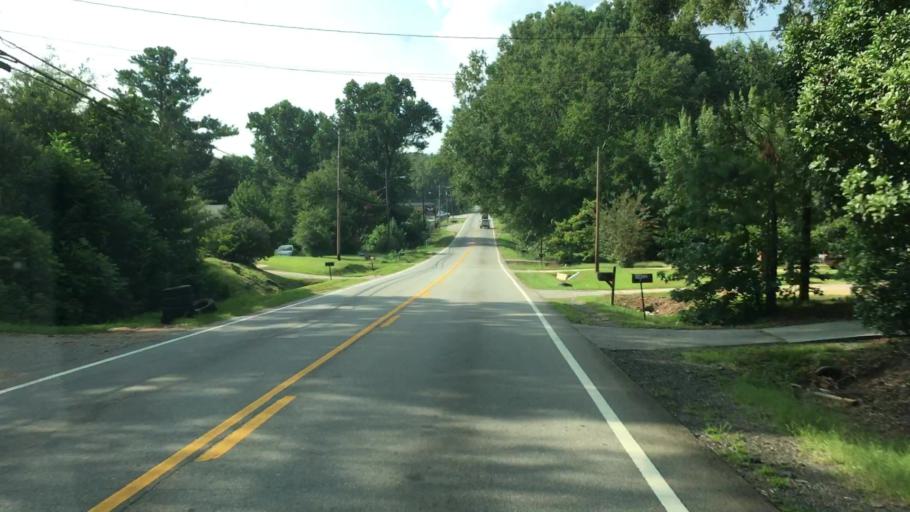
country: US
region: Georgia
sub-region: Walton County
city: Monroe
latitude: 33.7761
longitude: -83.7045
